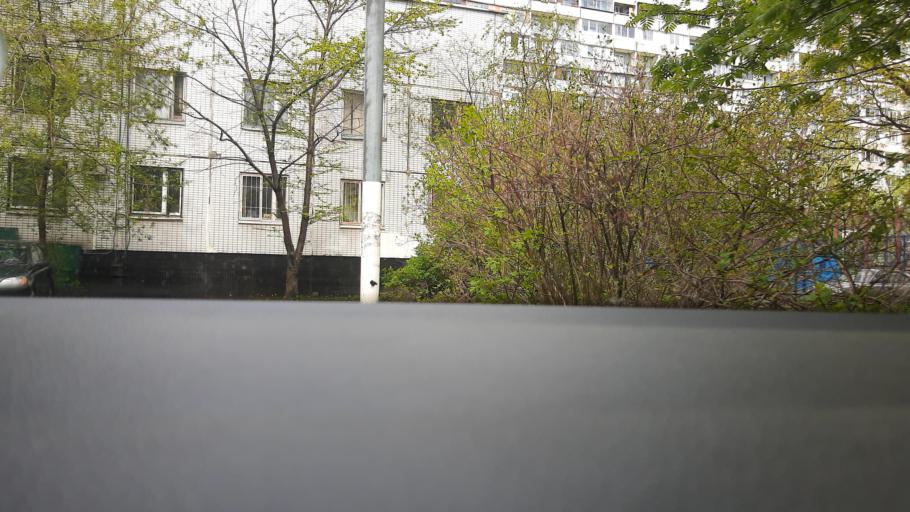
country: RU
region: Moscow
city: Ivanovskoye
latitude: 55.7792
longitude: 37.8263
